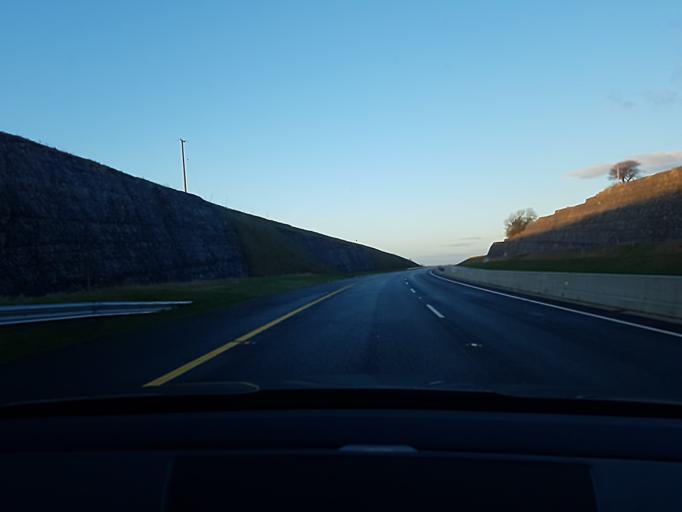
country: IE
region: Connaught
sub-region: County Galway
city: Tuam
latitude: 53.4479
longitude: -8.8498
